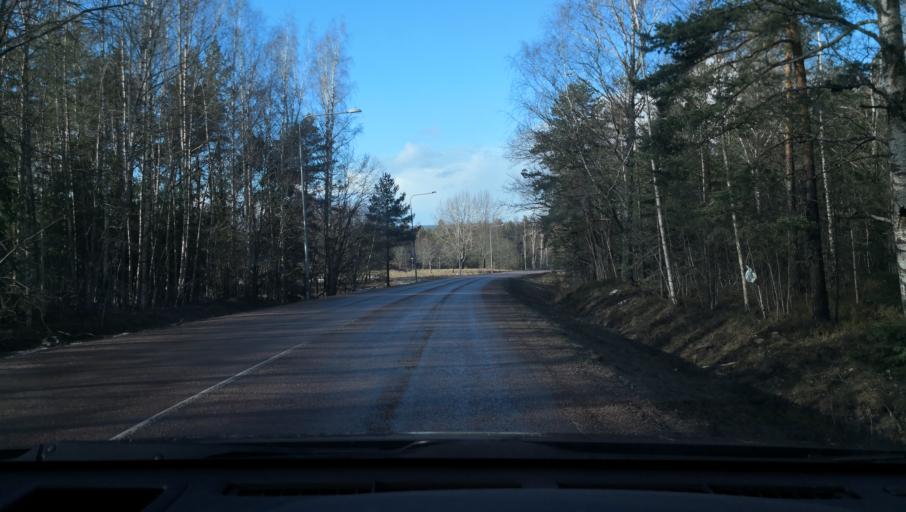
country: SE
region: Vaestmanland
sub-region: Arboga Kommun
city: Arboga
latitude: 59.3799
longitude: 15.8395
